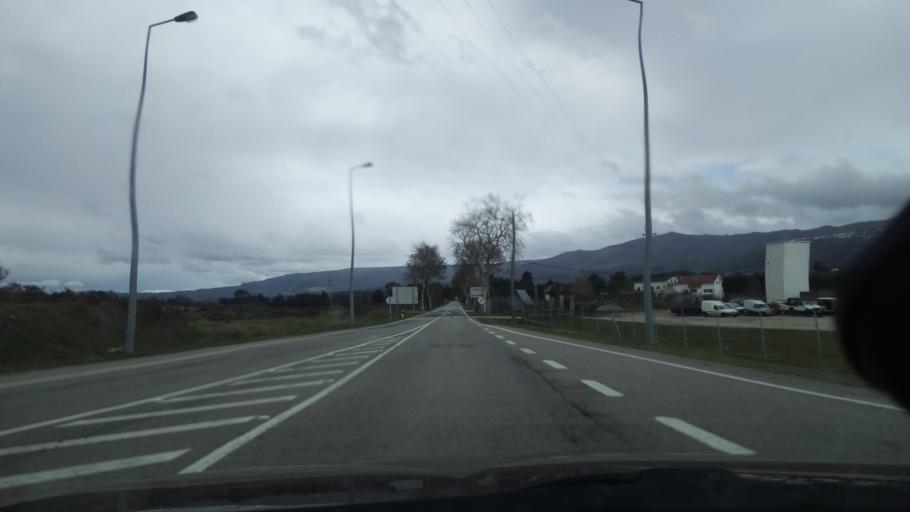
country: PT
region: Guarda
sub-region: Fornos de Algodres
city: Fornos de Algodres
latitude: 40.5360
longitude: -7.5616
